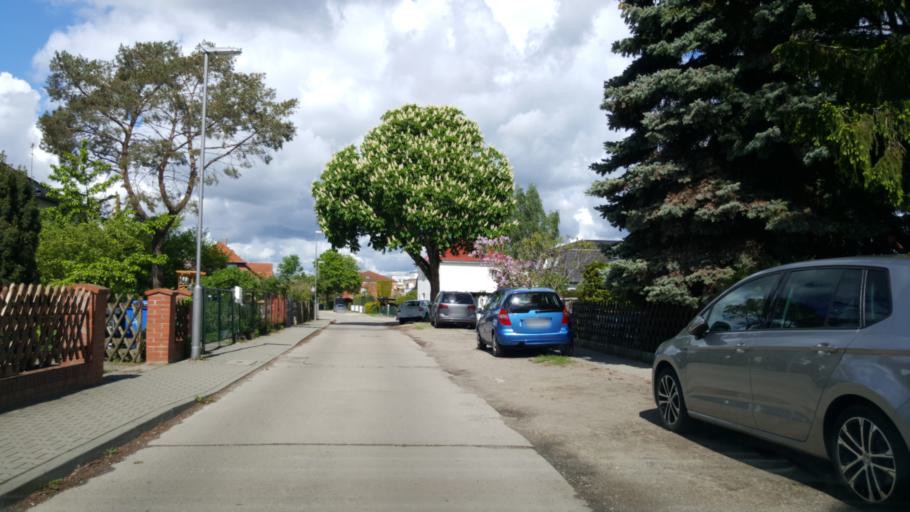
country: DE
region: Berlin
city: Altglienicke
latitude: 52.4180
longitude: 13.5329
